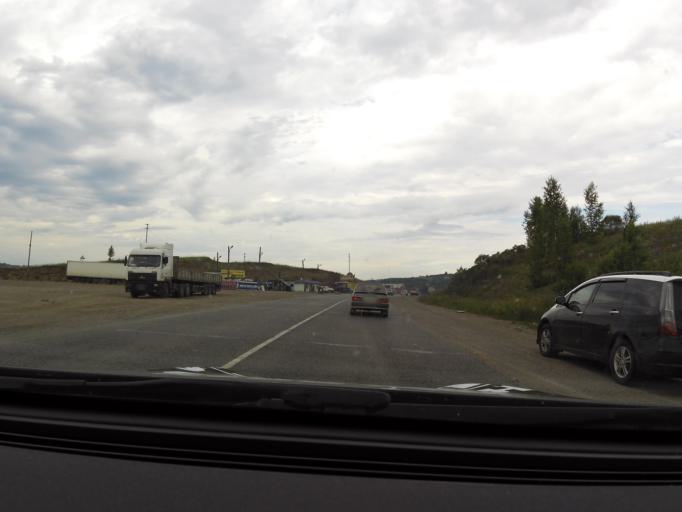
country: RU
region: Chelyabinsk
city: Sim
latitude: 54.9994
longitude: 57.6523
